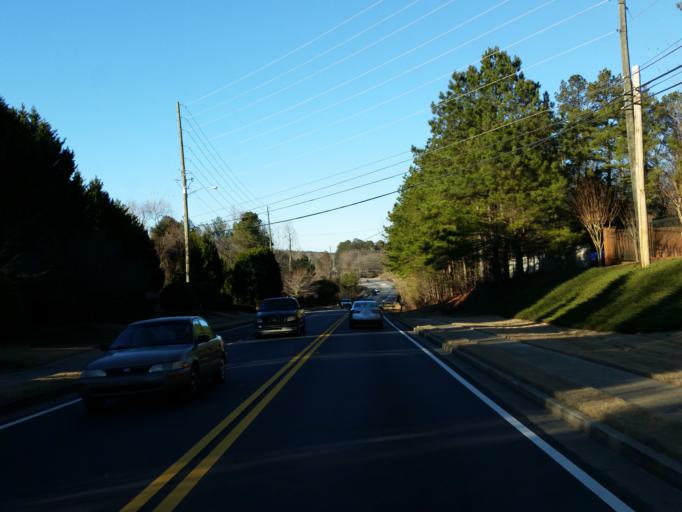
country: US
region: Georgia
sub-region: Cherokee County
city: Woodstock
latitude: 34.1015
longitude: -84.4703
